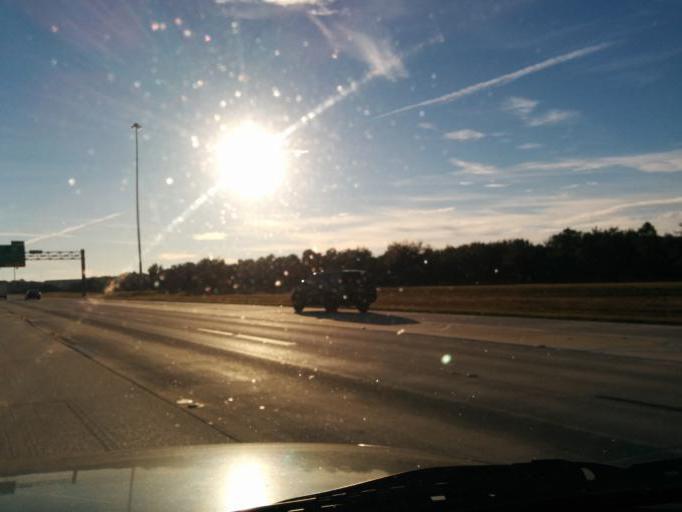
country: US
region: Florida
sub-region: Pinellas County
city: Feather Sound
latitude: 27.8894
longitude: -82.6493
